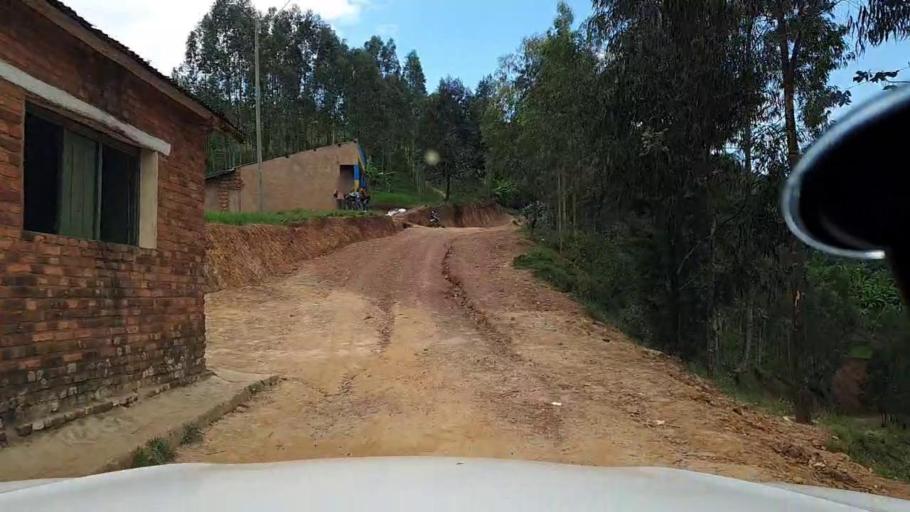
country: RW
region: Southern Province
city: Gitarama
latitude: -1.8018
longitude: 29.7937
